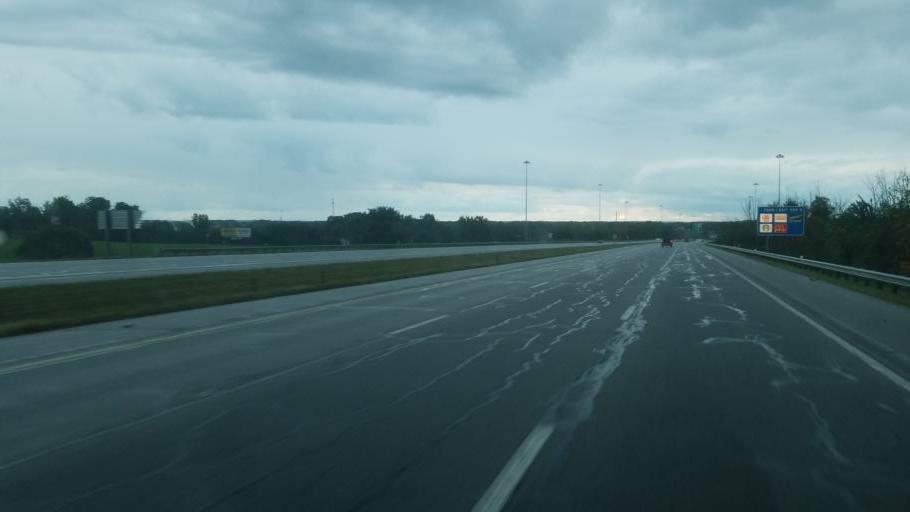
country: US
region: Ohio
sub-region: Medina County
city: Seville
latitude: 41.0408
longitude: -81.8755
